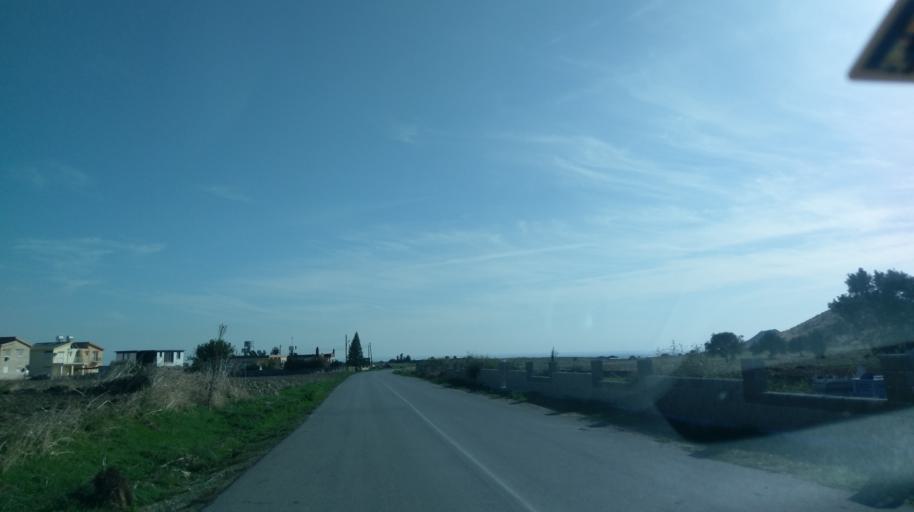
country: CY
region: Ammochostos
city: Trikomo
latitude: 35.3237
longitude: 33.8202
